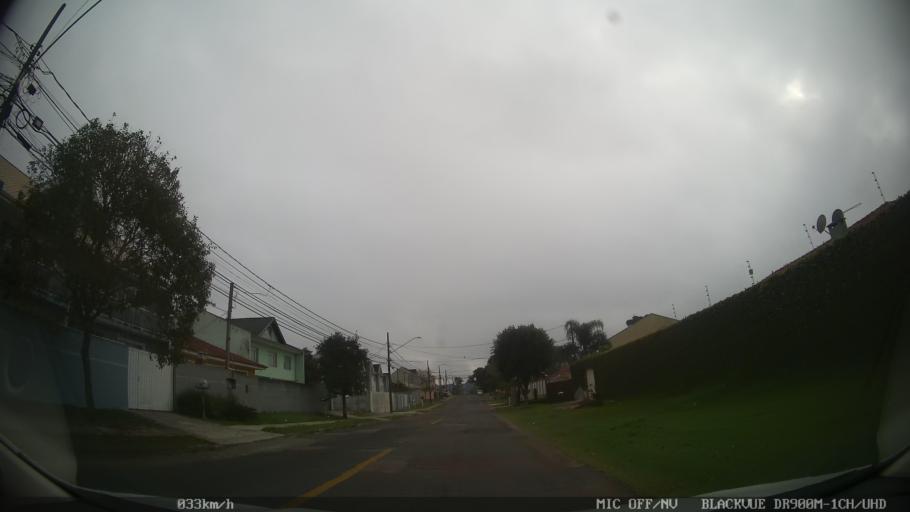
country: BR
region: Parana
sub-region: Almirante Tamandare
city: Almirante Tamandare
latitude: -25.3808
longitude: -49.3257
